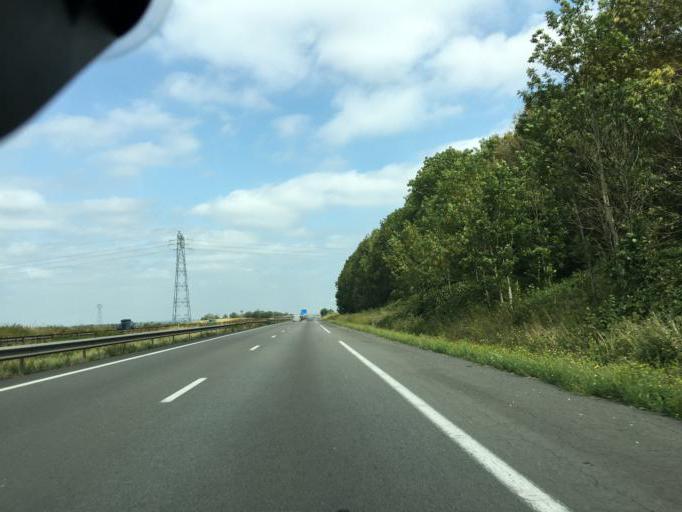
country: FR
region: Nord-Pas-de-Calais
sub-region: Departement du Nord
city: Onnaing
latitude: 50.3614
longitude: 3.5897
